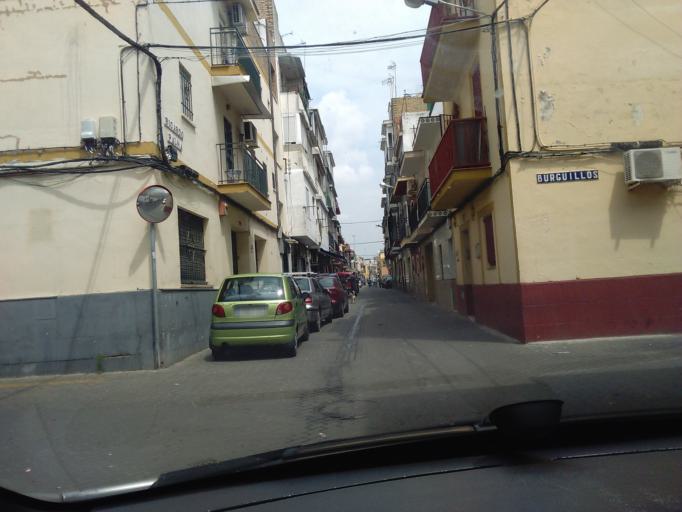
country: ES
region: Andalusia
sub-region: Provincia de Sevilla
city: Sevilla
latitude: 37.3696
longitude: -5.9460
